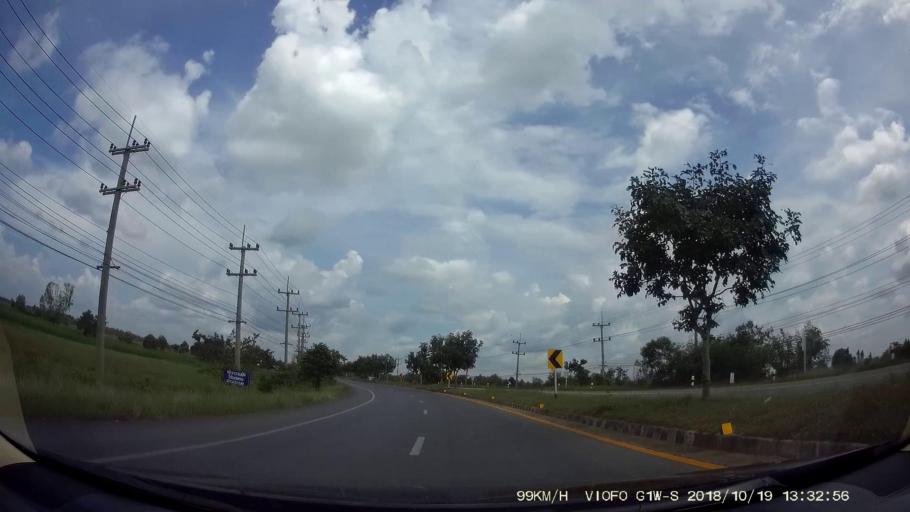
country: TH
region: Chaiyaphum
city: Chatturat
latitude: 15.5770
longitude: 101.8893
